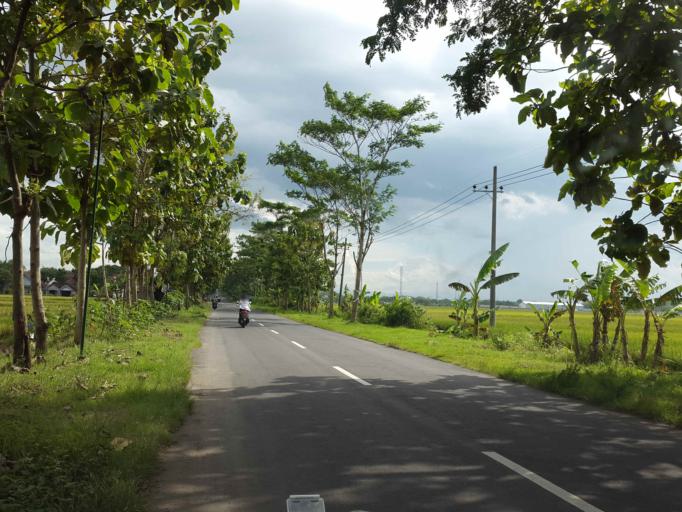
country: ID
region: East Java
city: Madiun
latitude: -7.5947
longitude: 111.5263
